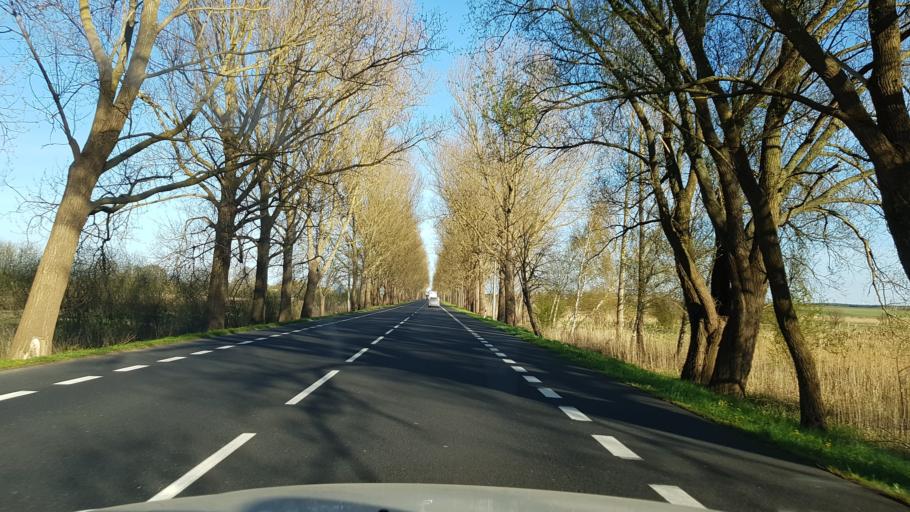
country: PL
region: West Pomeranian Voivodeship
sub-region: Powiat kamienski
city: Wolin
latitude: 53.8545
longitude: 14.5840
